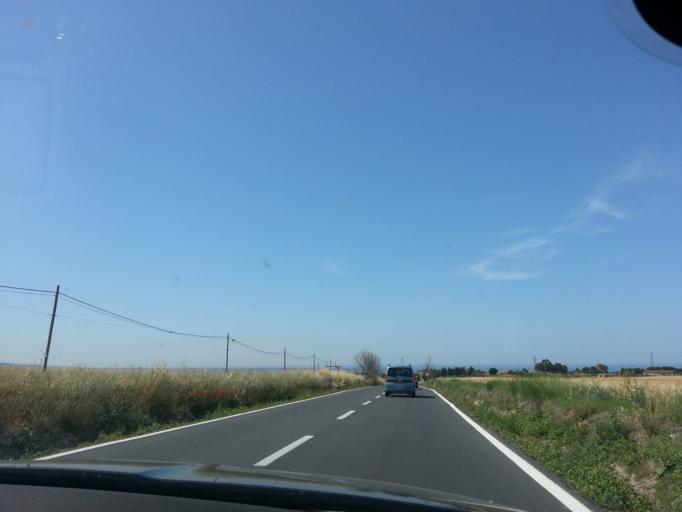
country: IT
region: Latium
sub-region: Provincia di Viterbo
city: Tarquinia
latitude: 42.2426
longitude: 11.8070
